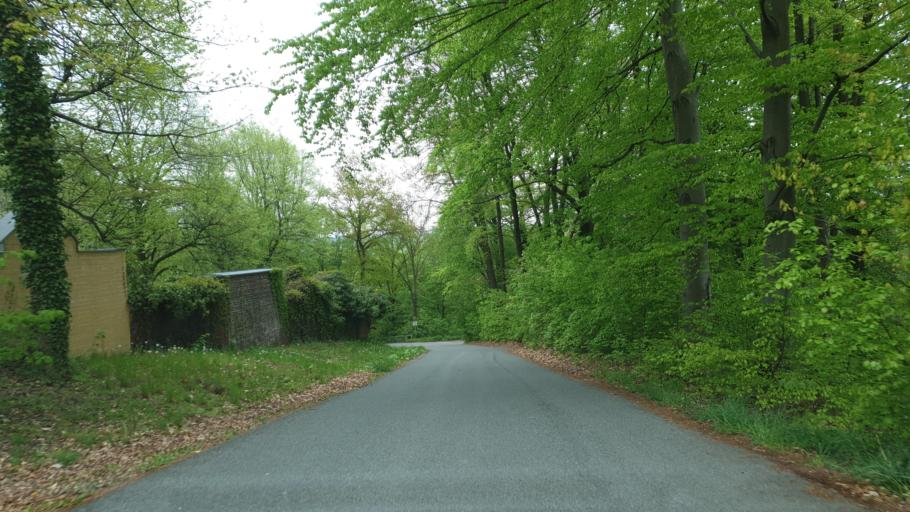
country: DE
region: Saxony
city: Oelsnitz
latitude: 50.7231
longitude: 12.6942
